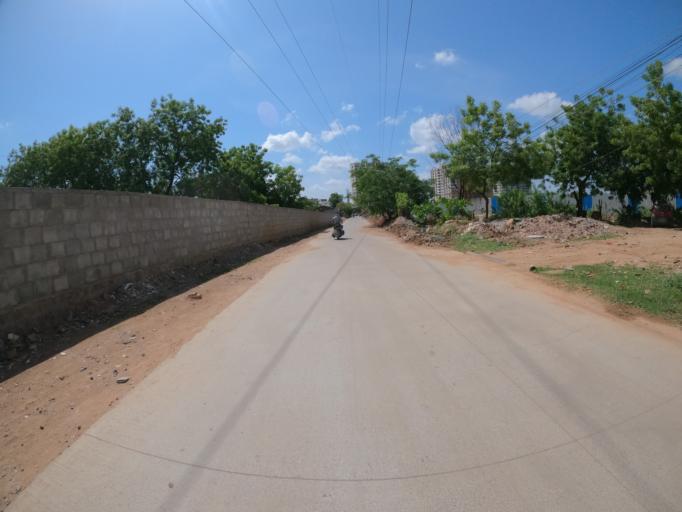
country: IN
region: Telangana
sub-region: Hyderabad
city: Hyderabad
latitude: 17.3582
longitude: 78.3820
